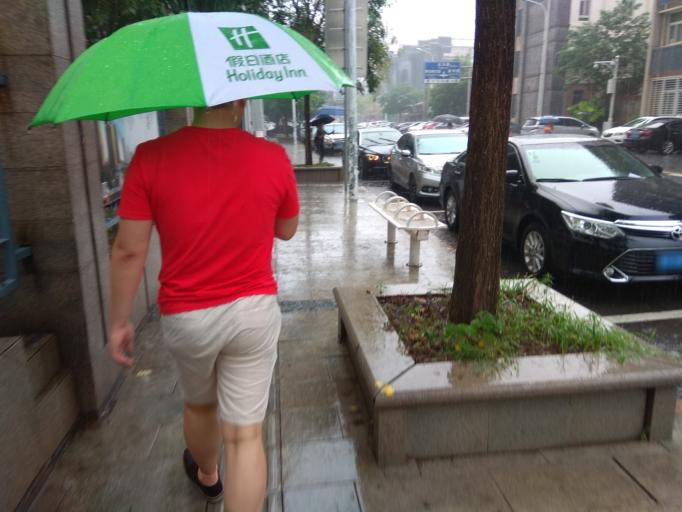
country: CN
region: Tianjin Shi
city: Hongshunli
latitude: 39.1521
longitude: 117.1869
